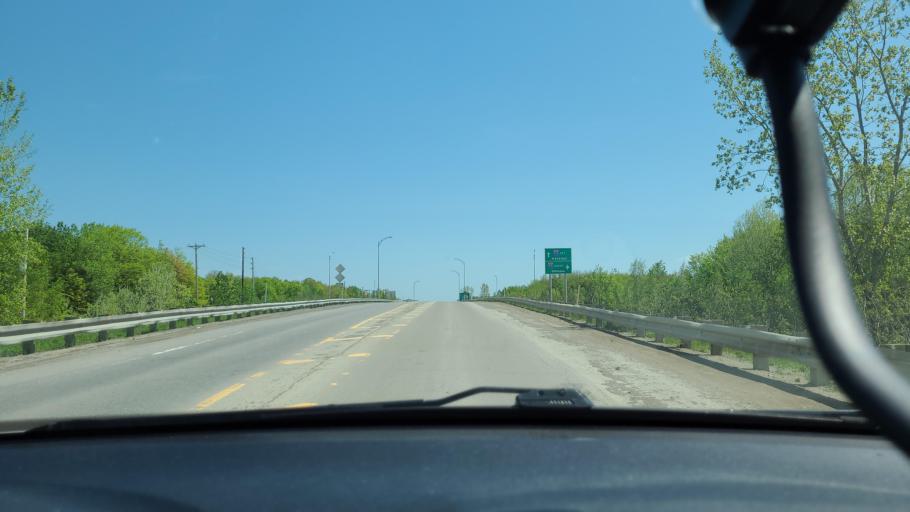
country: CA
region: Quebec
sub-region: Laurentides
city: Saint-Colomban
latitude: 45.6764
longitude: -74.1857
